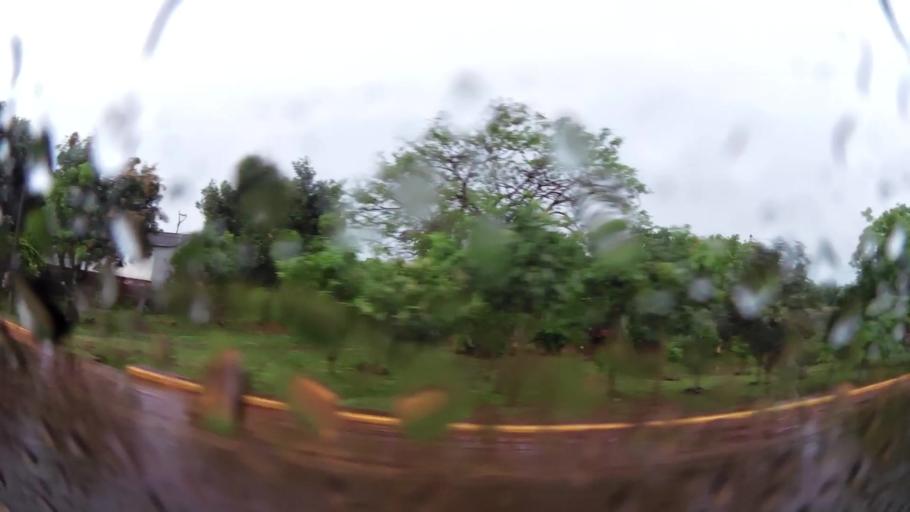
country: PY
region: Alto Parana
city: Presidente Franco
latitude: -25.5381
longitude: -54.6780
